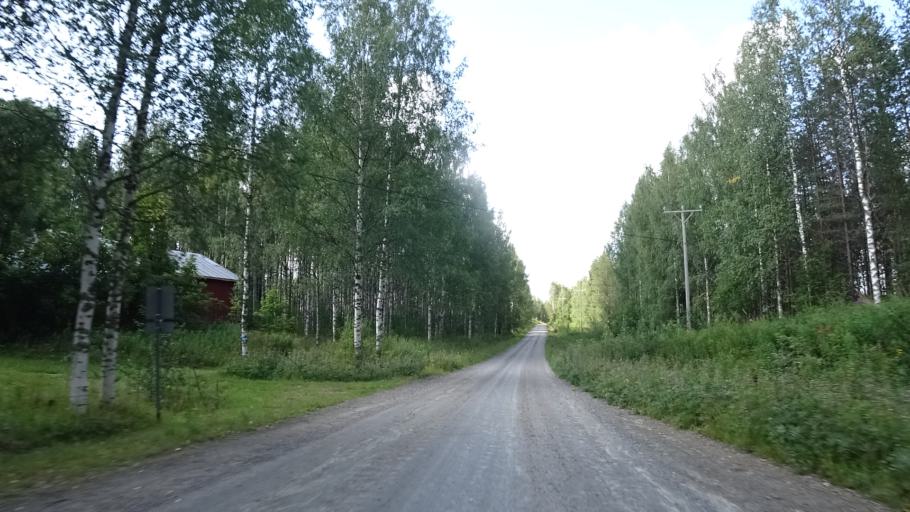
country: FI
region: North Karelia
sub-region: Joensuu
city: Ilomantsi
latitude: 62.9304
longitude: 31.3133
